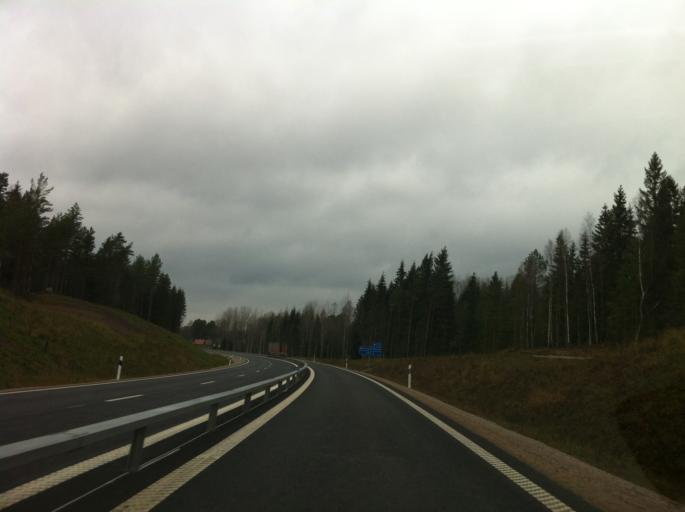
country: SE
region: Joenkoeping
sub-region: Vetlanda Kommun
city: Vetlanda
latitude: 57.4300
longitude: 15.1797
